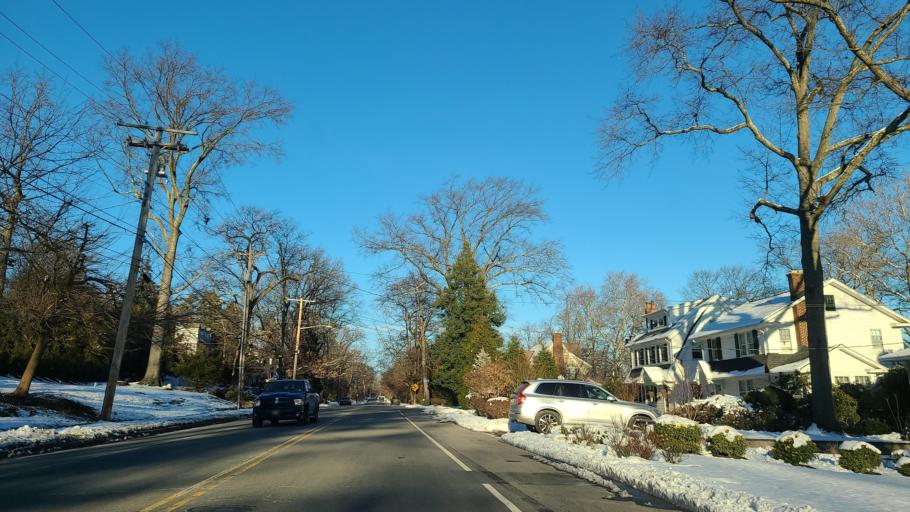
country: US
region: New Jersey
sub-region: Essex County
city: Maplewood
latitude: 40.7296
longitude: -74.2916
